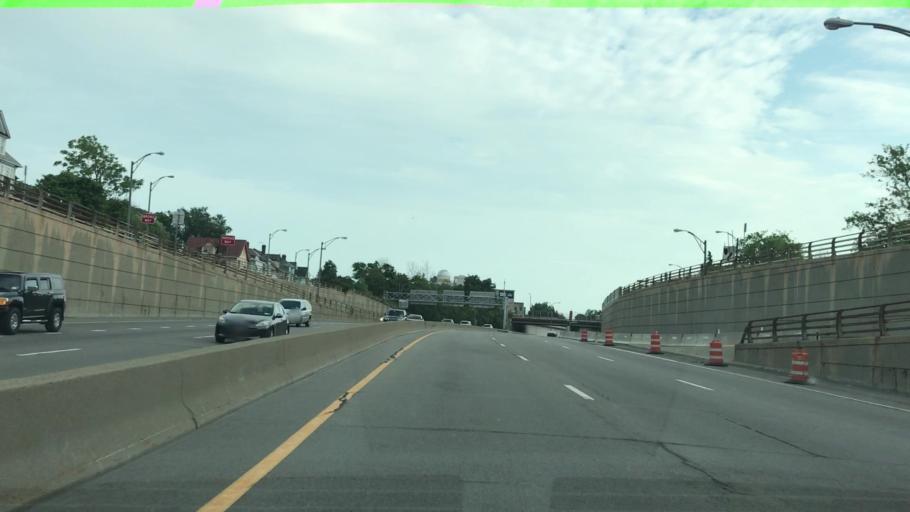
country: US
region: New York
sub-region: Erie County
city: Buffalo
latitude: 42.9098
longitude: -78.8435
